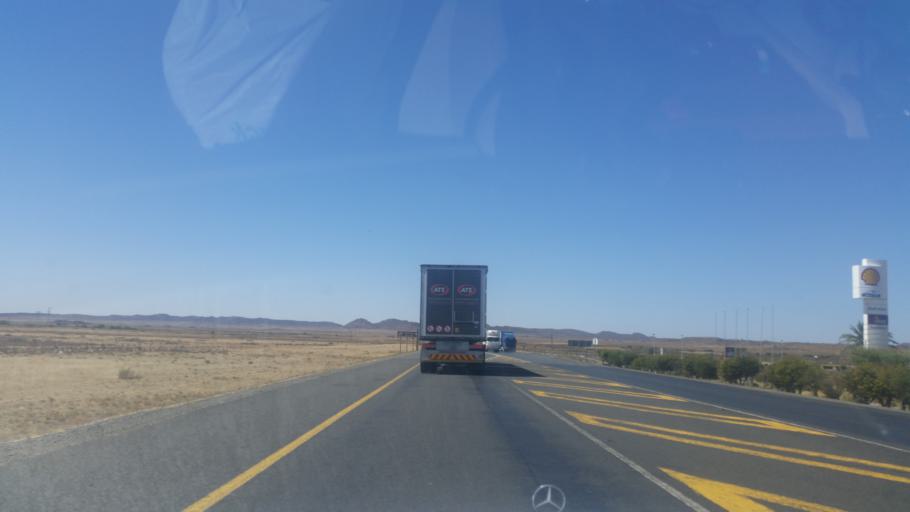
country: ZA
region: Northern Cape
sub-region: Pixley ka Seme District Municipality
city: Colesberg
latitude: -30.7005
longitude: 25.1254
